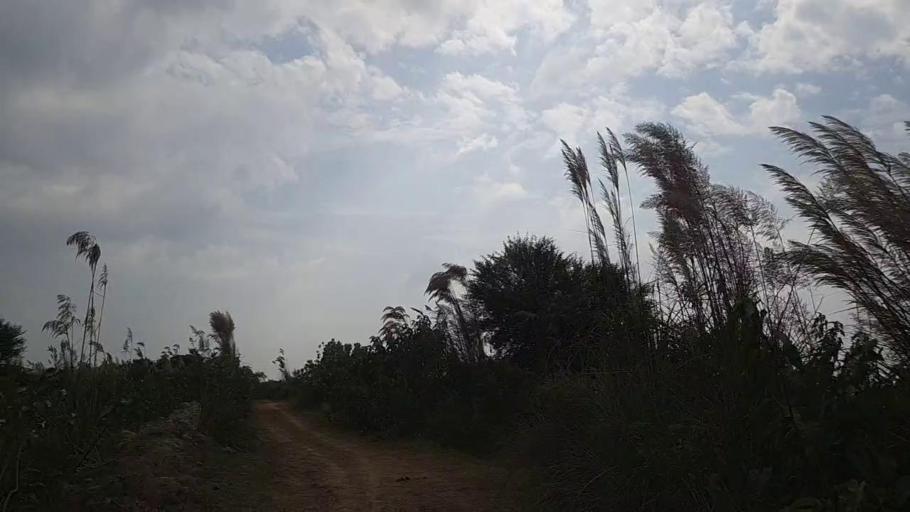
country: PK
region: Sindh
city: Mirpur Batoro
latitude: 24.6134
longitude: 68.1350
